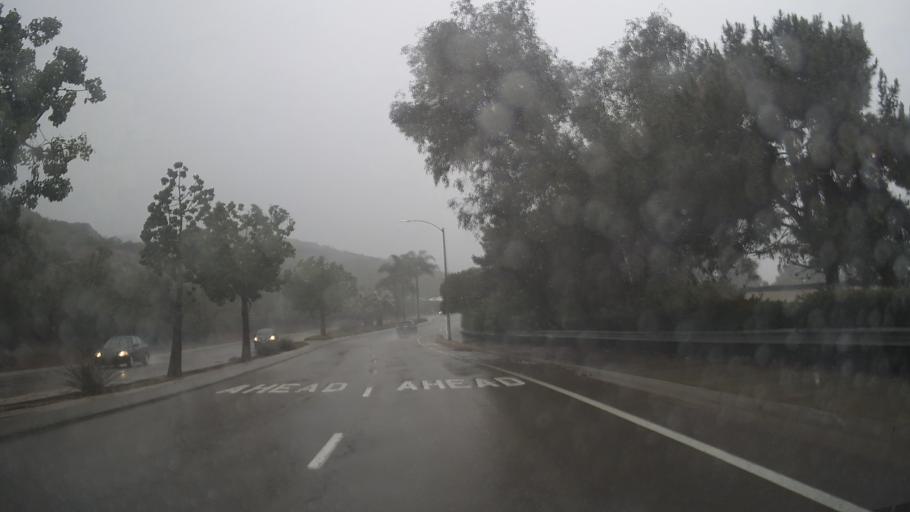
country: US
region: California
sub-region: San Diego County
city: Encinitas
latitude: 33.0666
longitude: -117.2672
